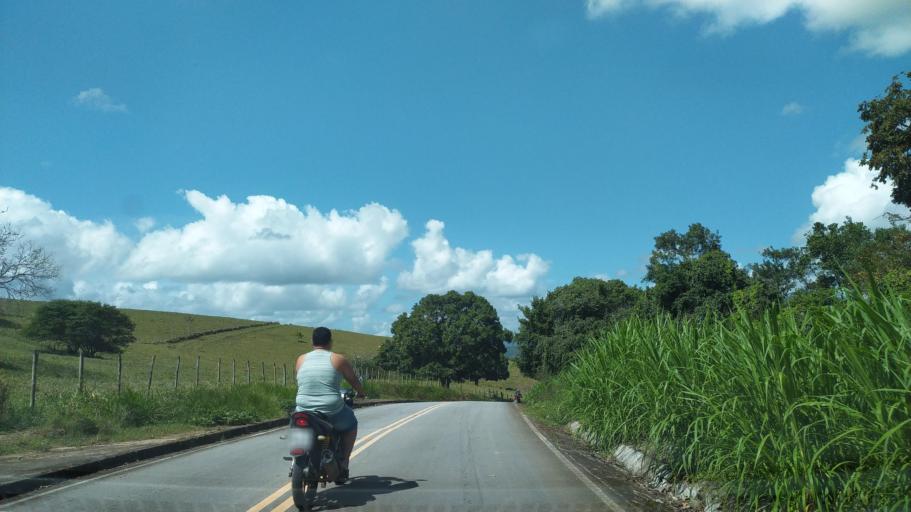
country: BR
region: Alagoas
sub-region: Uniao Dos Palmares
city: Uniao dos Palmares
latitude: -9.1625
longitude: -36.0685
